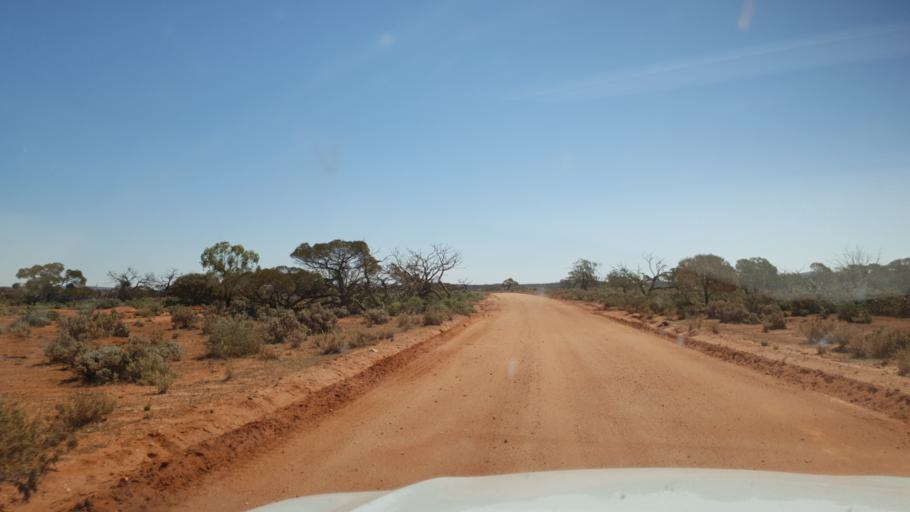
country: AU
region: South Australia
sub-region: Whyalla
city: Whyalla
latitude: -32.6270
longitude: 136.8266
